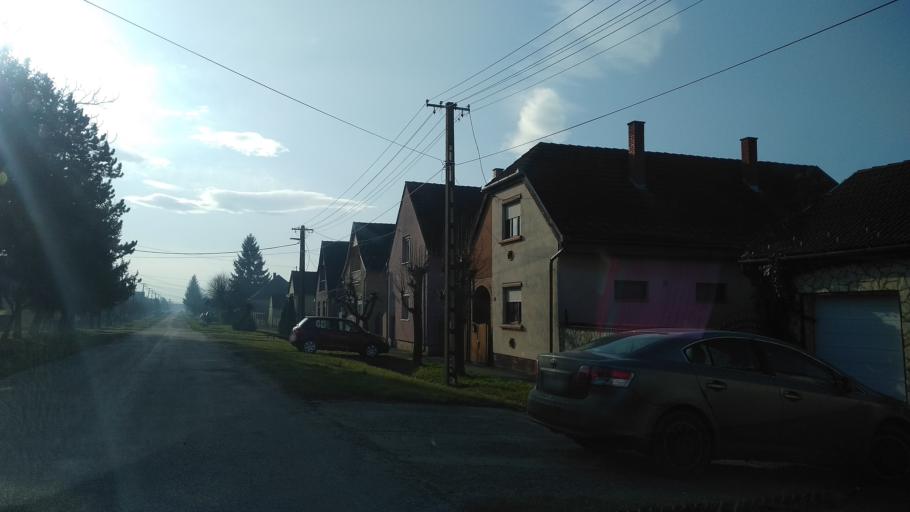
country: HU
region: Somogy
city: Barcs
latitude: 45.9663
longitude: 17.4739
